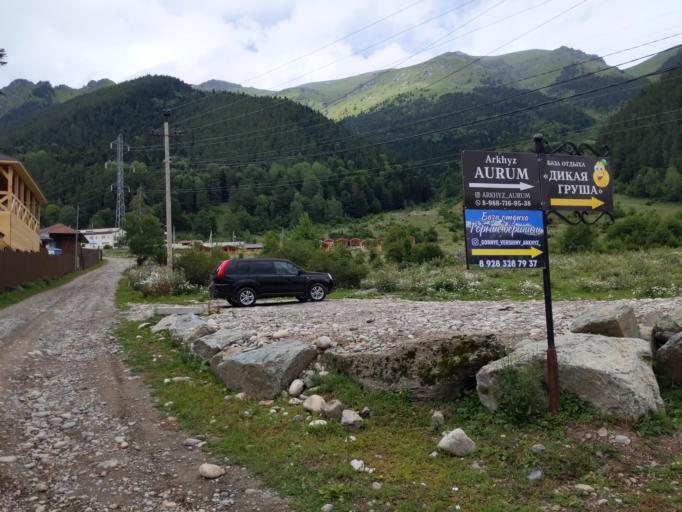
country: RU
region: Karachayevo-Cherkesiya
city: Nizhniy Arkhyz
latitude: 43.5665
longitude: 41.2684
